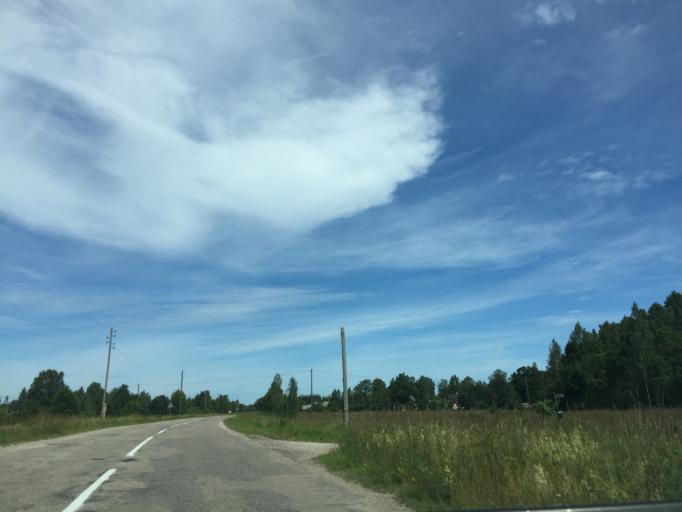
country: LV
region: Dundaga
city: Dundaga
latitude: 57.5226
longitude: 22.3326
